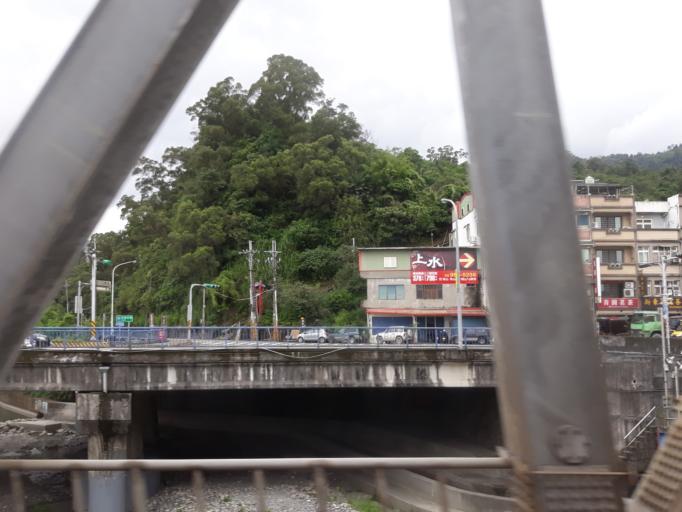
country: TW
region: Taiwan
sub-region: Yilan
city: Yilan
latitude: 24.6158
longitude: 121.8121
